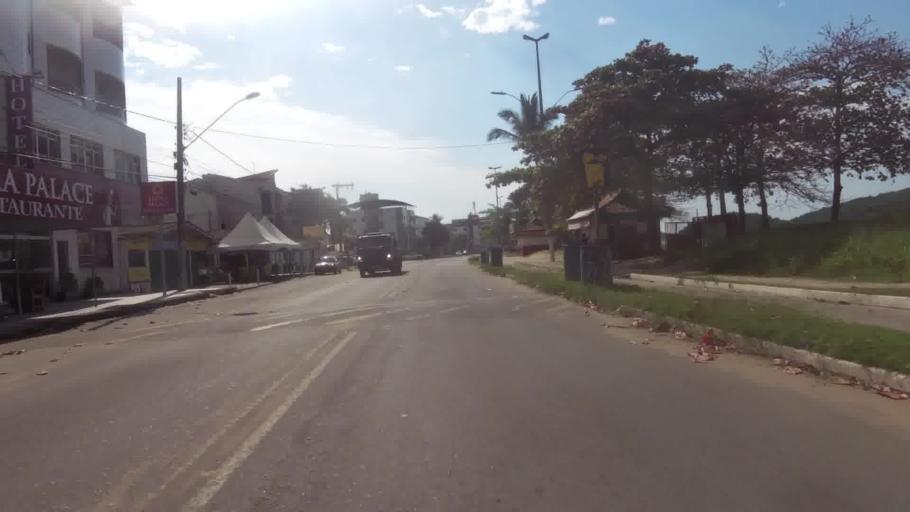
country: BR
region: Espirito Santo
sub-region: Piuma
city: Piuma
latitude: -20.8422
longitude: -40.7295
